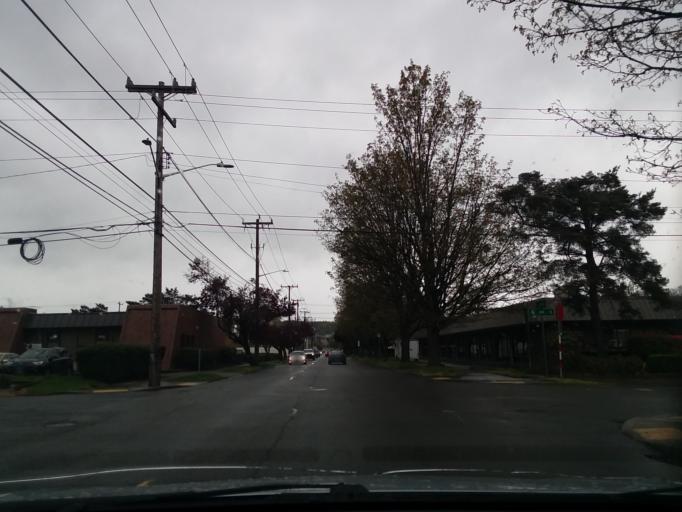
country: US
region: Washington
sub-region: King County
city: White Center
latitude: 47.5534
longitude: -122.3267
